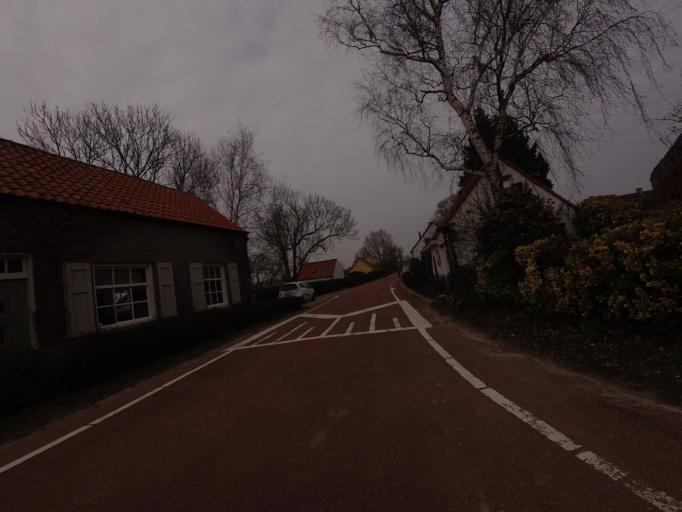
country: NL
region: Zeeland
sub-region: Gemeente Hulst
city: Hulst
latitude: 51.3515
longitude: 4.0952
